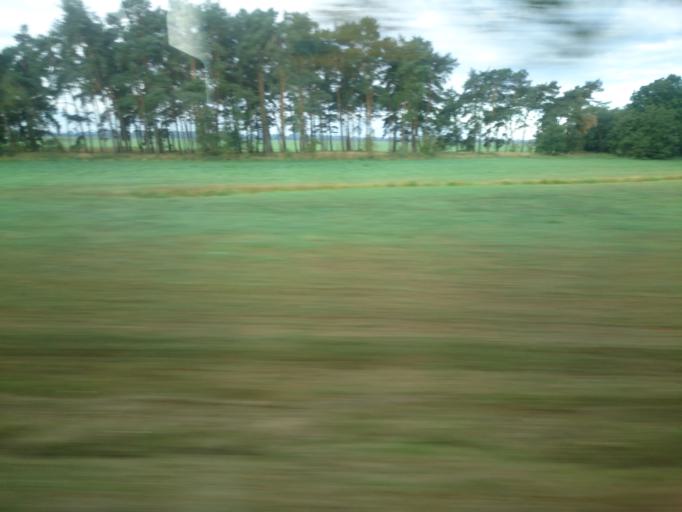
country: DE
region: Mecklenburg-Vorpommern
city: Ferdinandshof
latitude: 53.6891
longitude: 13.8798
